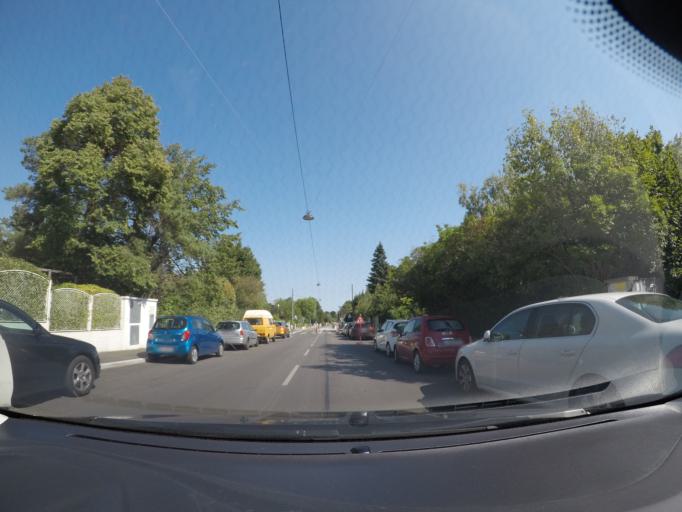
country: AT
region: Lower Austria
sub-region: Politischer Bezirk Modling
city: Perchtoldsdorf
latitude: 48.1591
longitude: 16.2653
